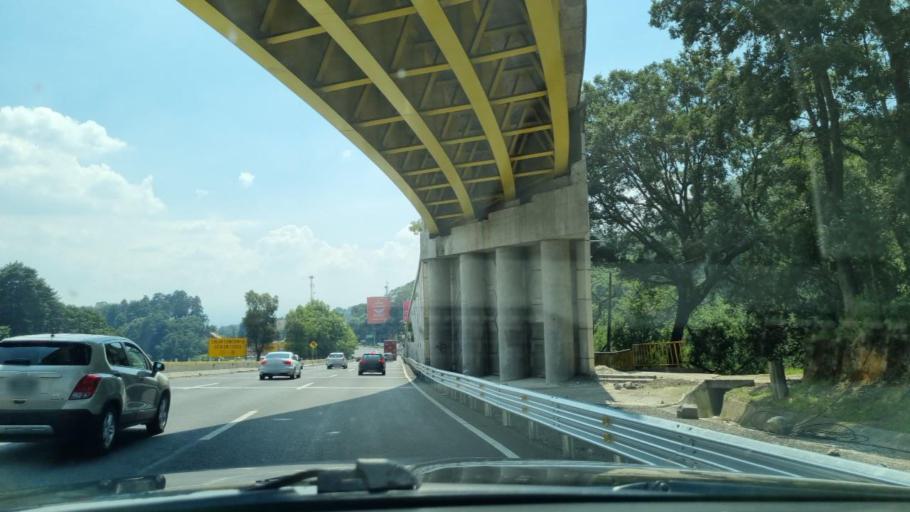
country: MX
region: Morelos
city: San Jeronimo Acazulco
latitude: 19.2924
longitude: -99.4278
